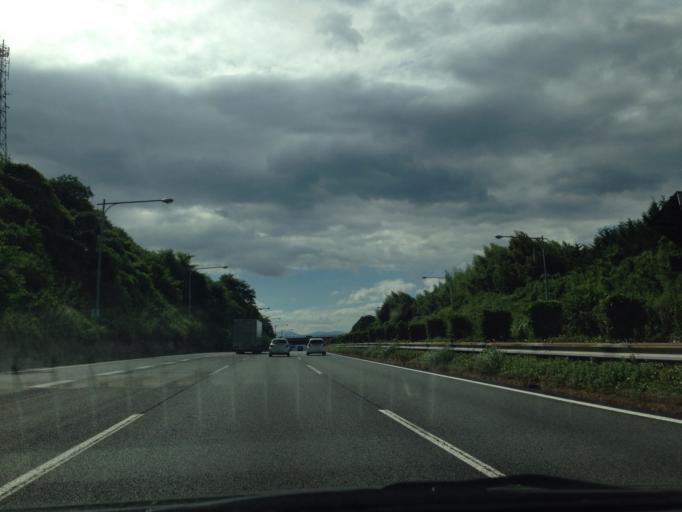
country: JP
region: Kanagawa
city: Hadano
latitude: 35.3383
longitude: 139.1763
